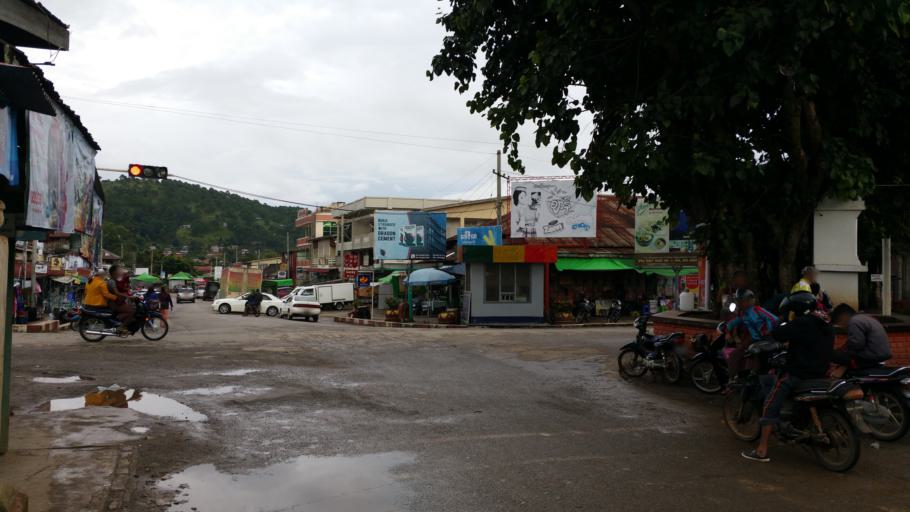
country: MM
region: Mandalay
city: Yamethin
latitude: 20.6353
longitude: 96.5663
